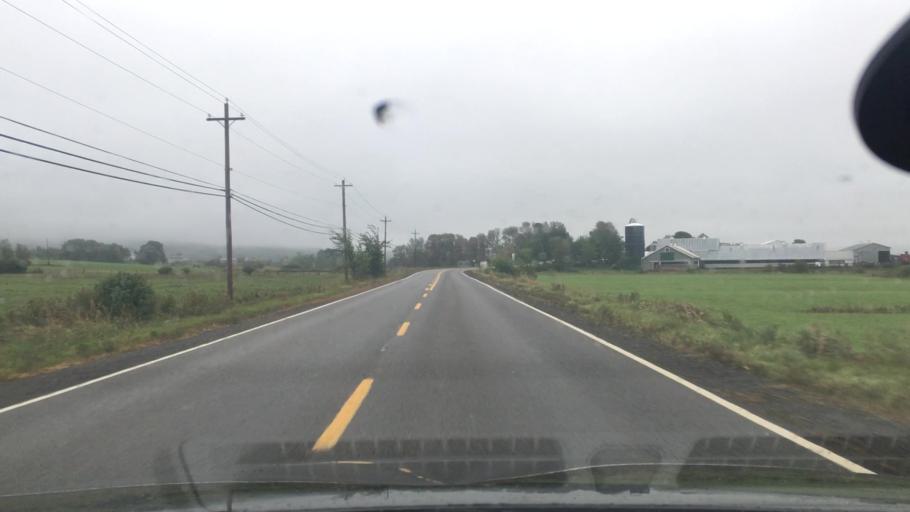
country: CA
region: Nova Scotia
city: Windsor
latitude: 44.9715
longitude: -64.1394
